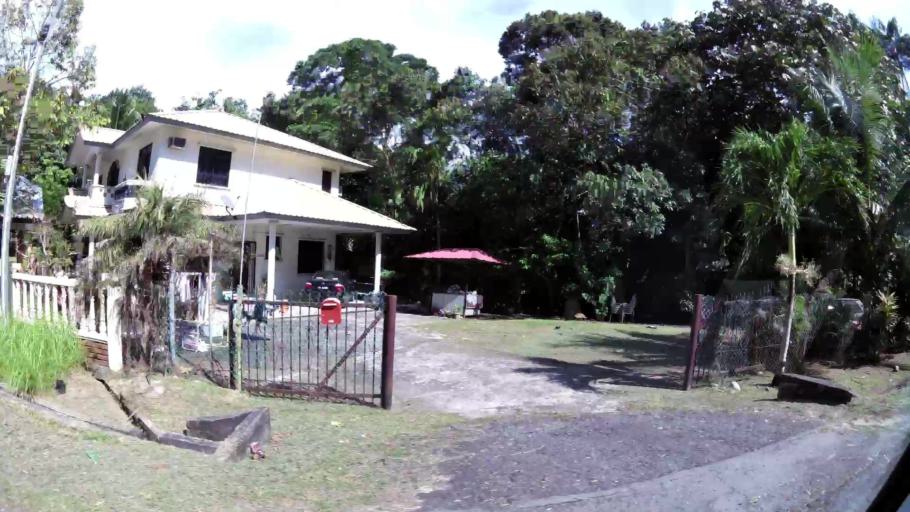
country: BN
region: Brunei and Muara
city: Bandar Seri Begawan
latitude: 5.0259
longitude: 115.0428
